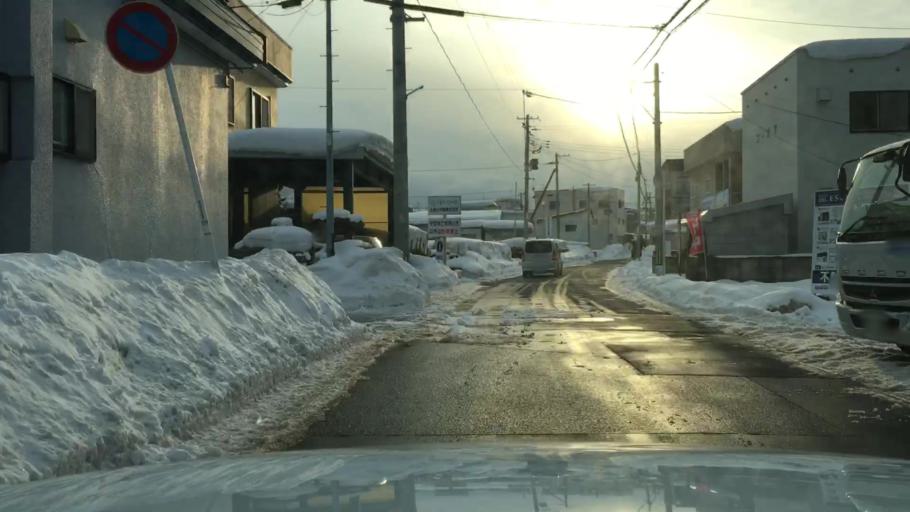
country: JP
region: Aomori
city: Hirosaki
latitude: 40.5859
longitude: 140.4785
